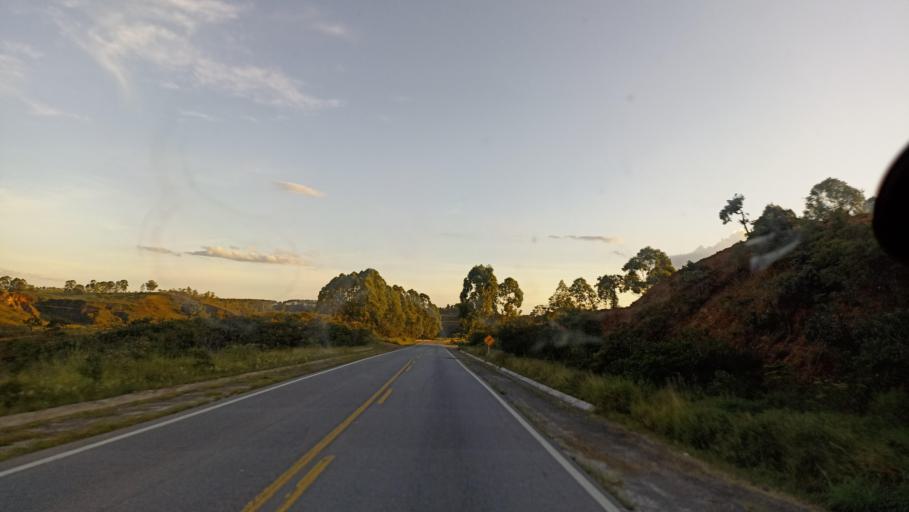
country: BR
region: Minas Gerais
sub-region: Sao Joao Del Rei
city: Sao Joao del Rei
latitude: -21.2206
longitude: -44.3601
